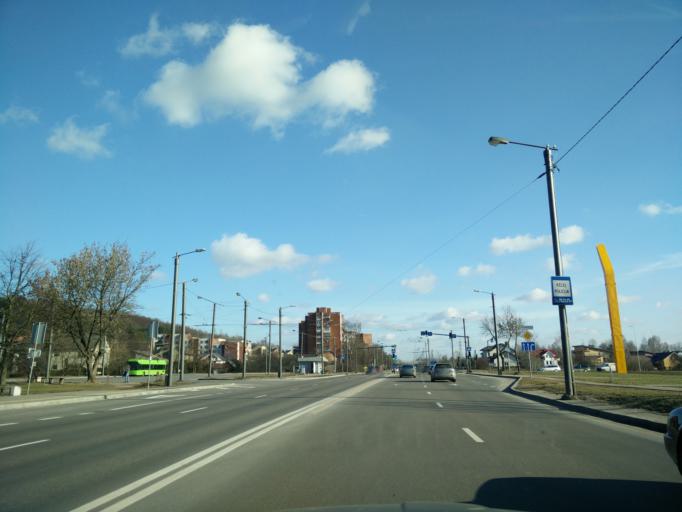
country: LT
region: Kauno apskritis
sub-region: Kauno rajonas
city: Akademija (Kaunas)
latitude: 54.9197
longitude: 23.8280
